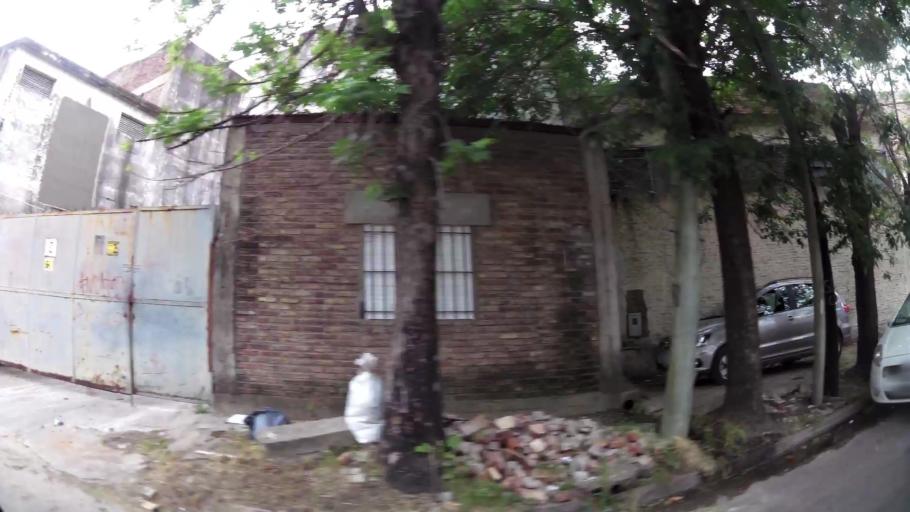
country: AR
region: Buenos Aires
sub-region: Partido de Lanus
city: Lanus
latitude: -34.6808
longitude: -58.3828
